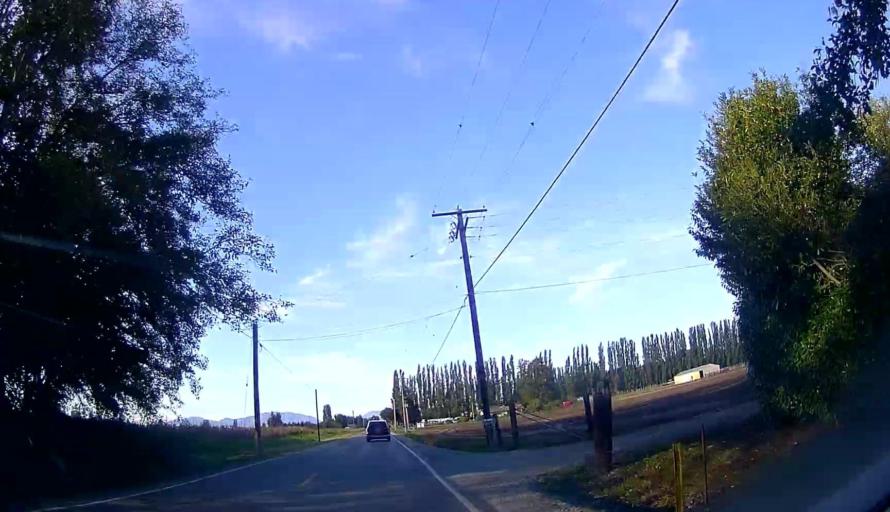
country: US
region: Washington
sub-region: Skagit County
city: Burlington
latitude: 48.4600
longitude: -122.3570
